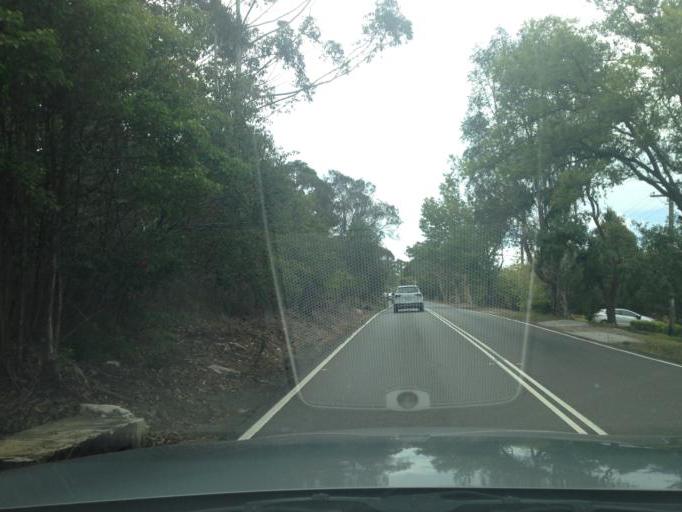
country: AU
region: New South Wales
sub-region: Ku-ring-gai
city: Lindfield
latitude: -33.7800
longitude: 151.1520
